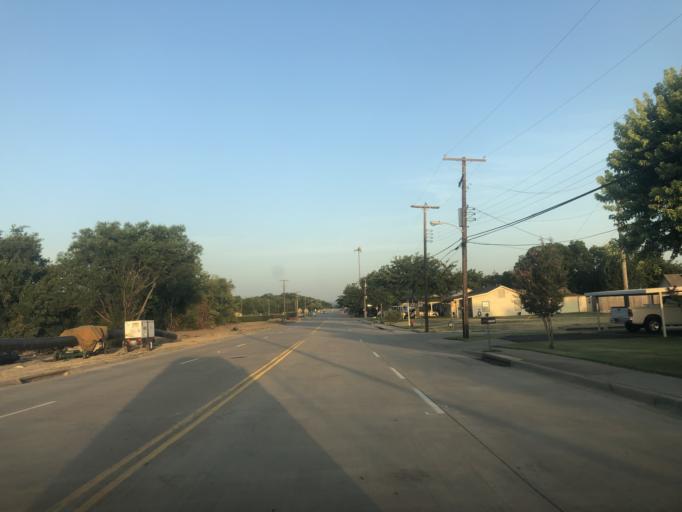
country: US
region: Texas
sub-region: Tarrant County
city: Lake Worth
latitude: 32.8106
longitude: -97.4332
